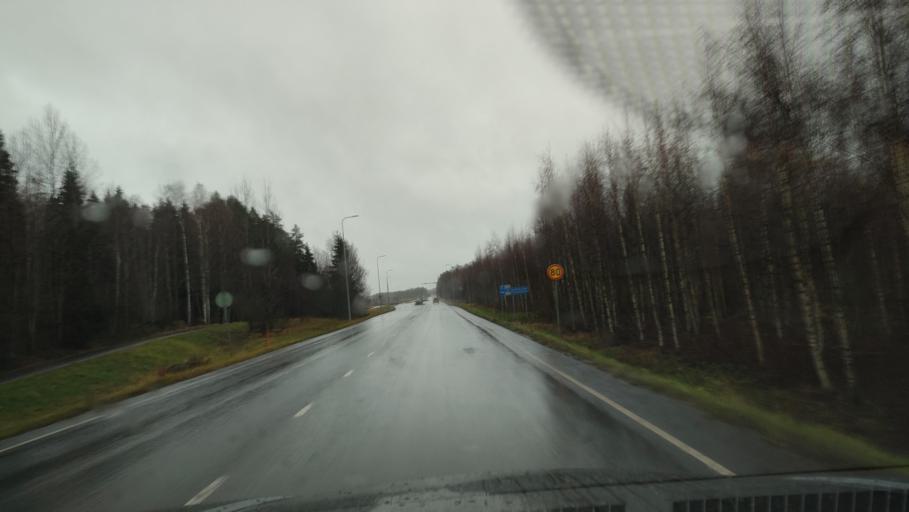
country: FI
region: Ostrobothnia
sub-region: Vaasa
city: Ristinummi
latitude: 63.0506
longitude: 21.7255
